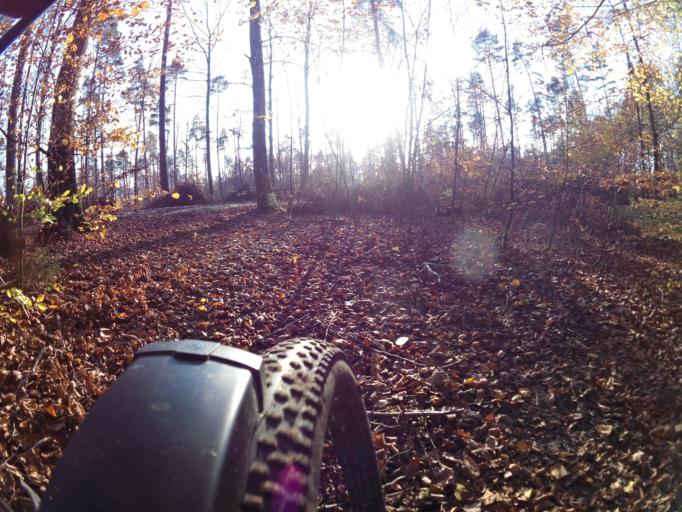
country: PL
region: Pomeranian Voivodeship
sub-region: Powiat pucki
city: Krokowa
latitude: 54.7290
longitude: 18.2060
